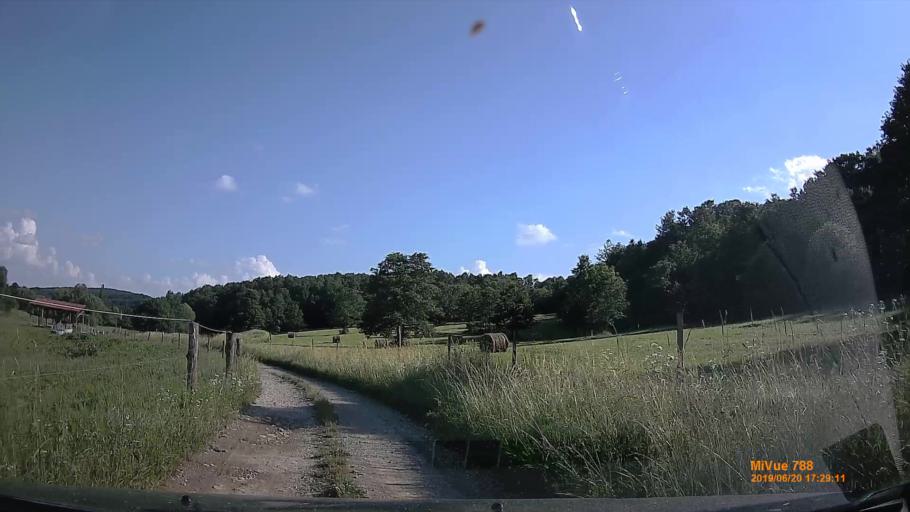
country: HU
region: Baranya
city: Buekkoesd
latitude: 46.1570
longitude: 18.0098
